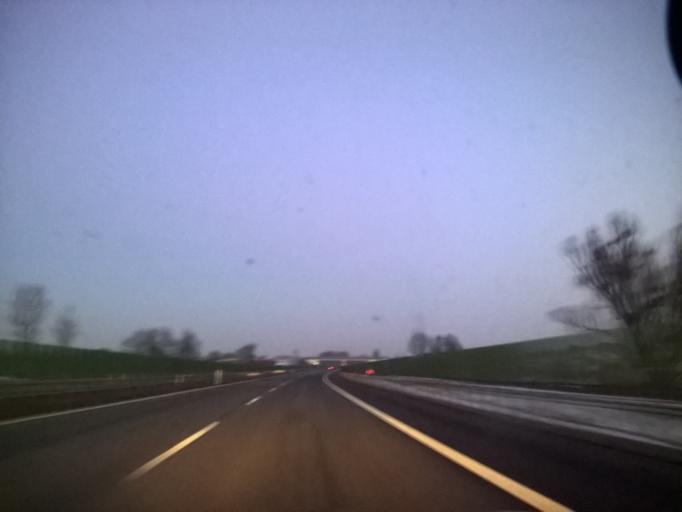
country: PL
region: Warmian-Masurian Voivodeship
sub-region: Powiat olsztynski
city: Biskupiec
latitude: 53.8406
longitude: 21.0112
